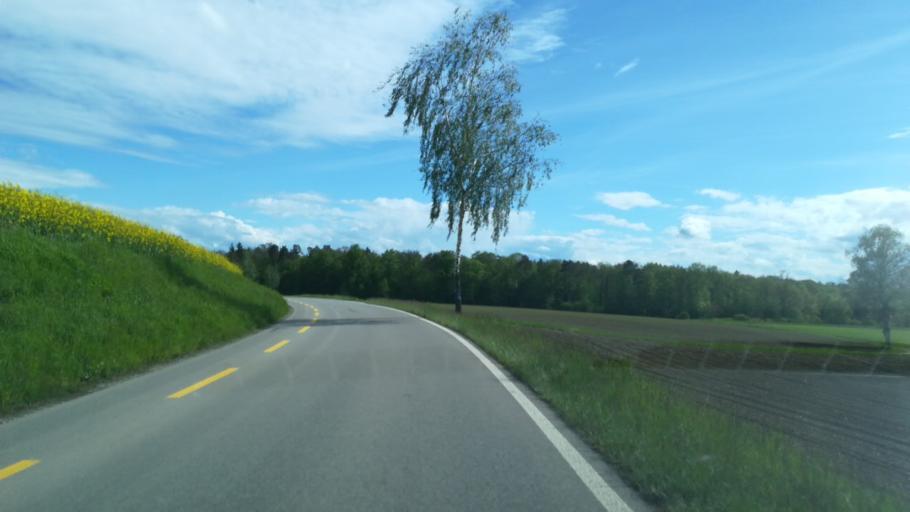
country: CH
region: Schaffhausen
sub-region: Bezirk Reiat
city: Thayngen
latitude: 47.7262
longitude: 8.7105
